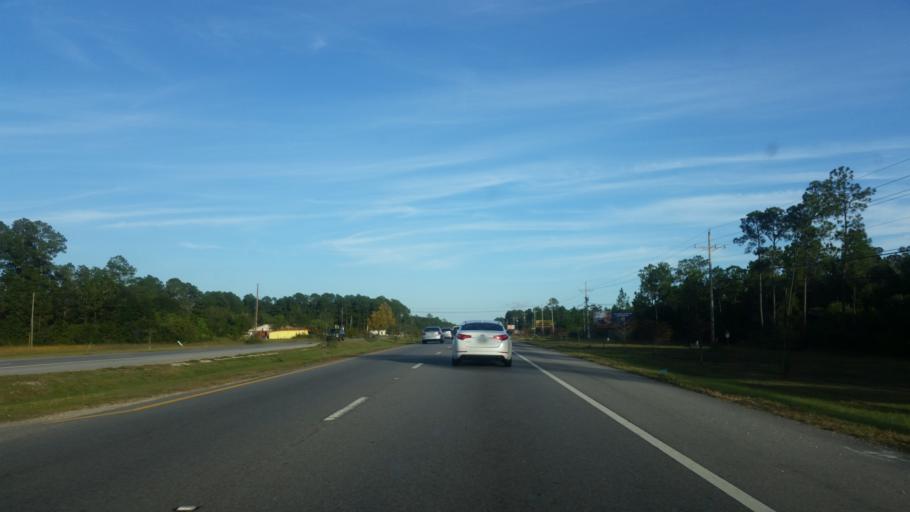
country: US
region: Mississippi
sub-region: Jackson County
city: Gulf Park Estates
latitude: 30.4061
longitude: -88.7423
